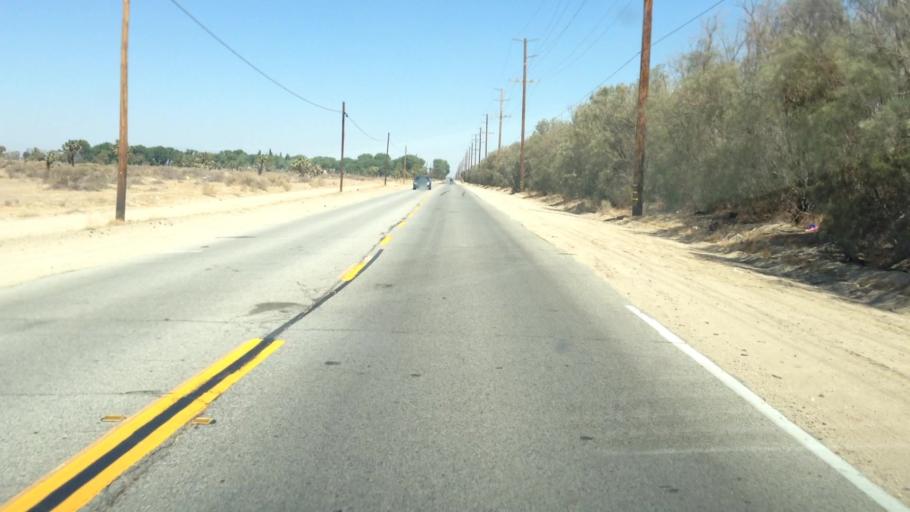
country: US
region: California
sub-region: Los Angeles County
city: Palmdale
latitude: 34.5888
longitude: -118.0585
